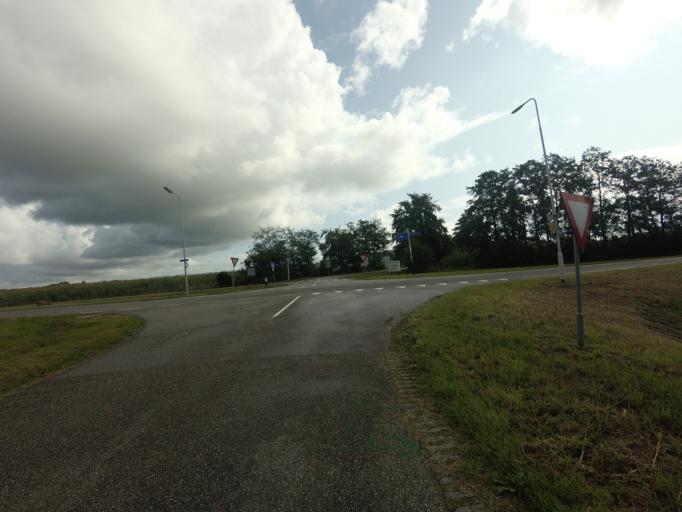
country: NL
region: Friesland
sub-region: Gemeente Tytsjerksteradiel
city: Garyp
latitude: 53.1544
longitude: 5.9513
